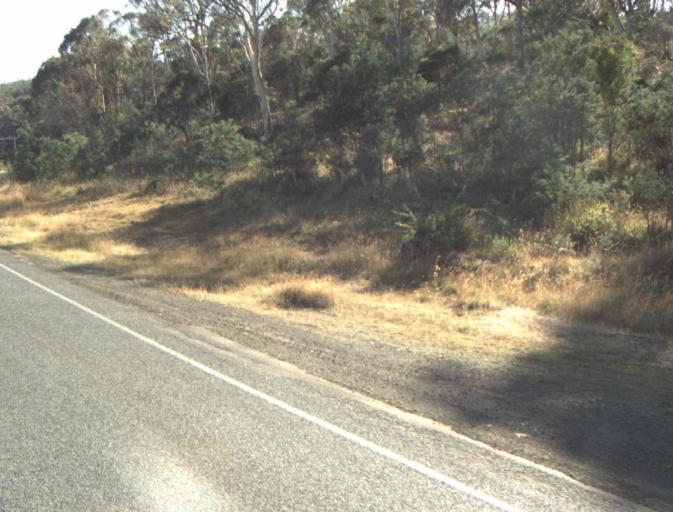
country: AU
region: Tasmania
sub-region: Launceston
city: Newstead
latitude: -41.4293
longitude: 147.2524
